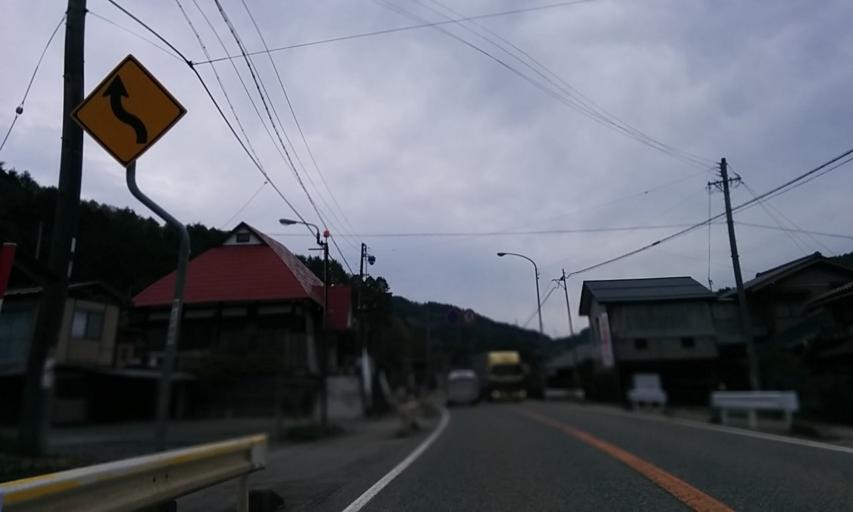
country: JP
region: Gifu
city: Takayama
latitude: 36.0585
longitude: 137.2720
